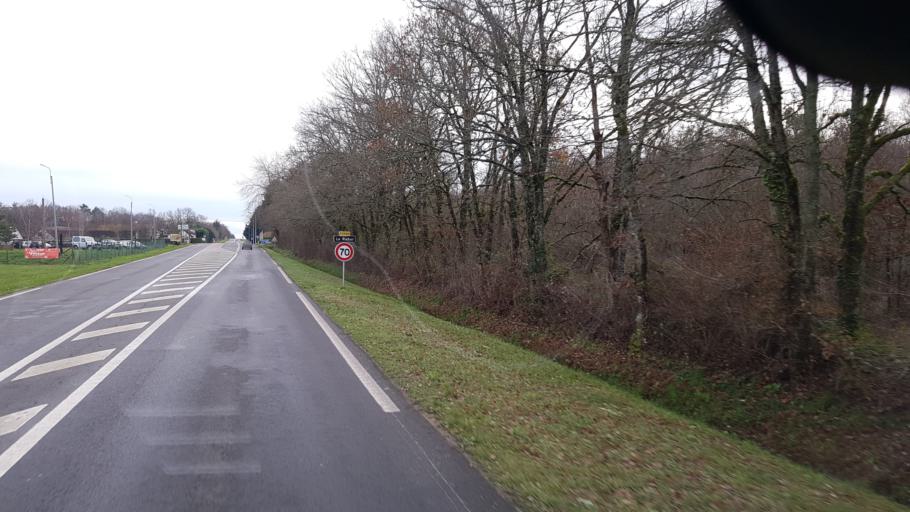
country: FR
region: Centre
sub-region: Departement du Loiret
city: Menestreau-en-Villette
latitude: 47.6541
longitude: 1.9863
